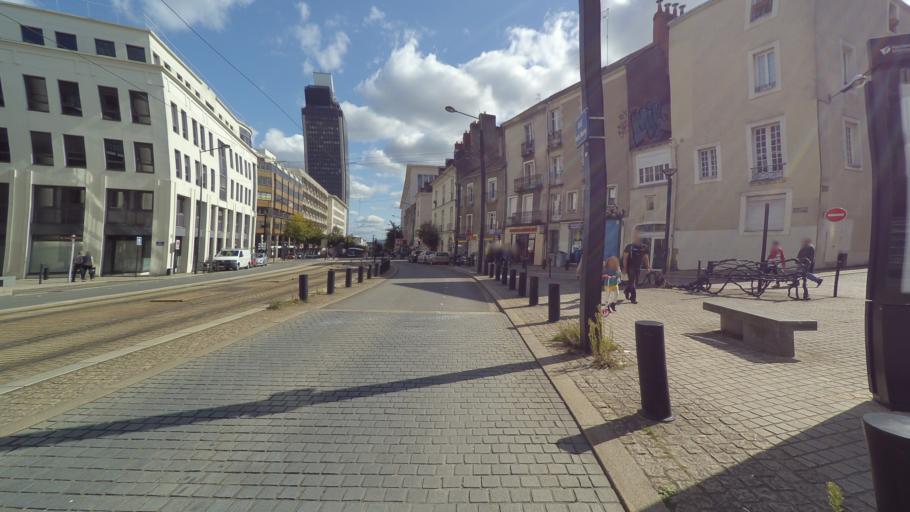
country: FR
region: Pays de la Loire
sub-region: Departement de la Loire-Atlantique
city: Nantes
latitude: 47.2193
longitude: -1.5615
